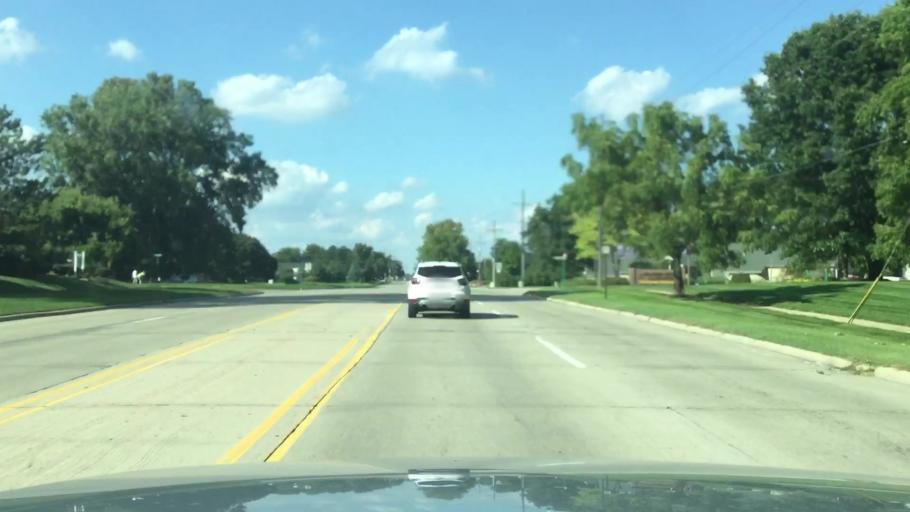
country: US
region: Michigan
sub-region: Wayne County
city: Westland
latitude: 42.3403
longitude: -83.4094
